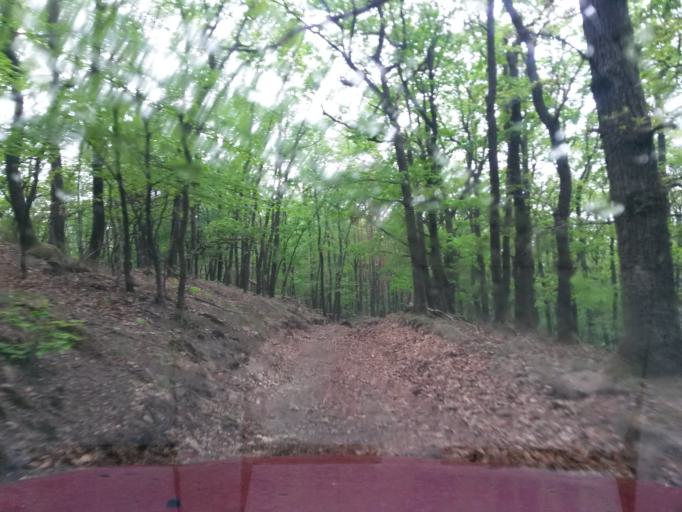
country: HU
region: Borsod-Abauj-Zemplen
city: Gonc
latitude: 48.5129
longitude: 21.3459
